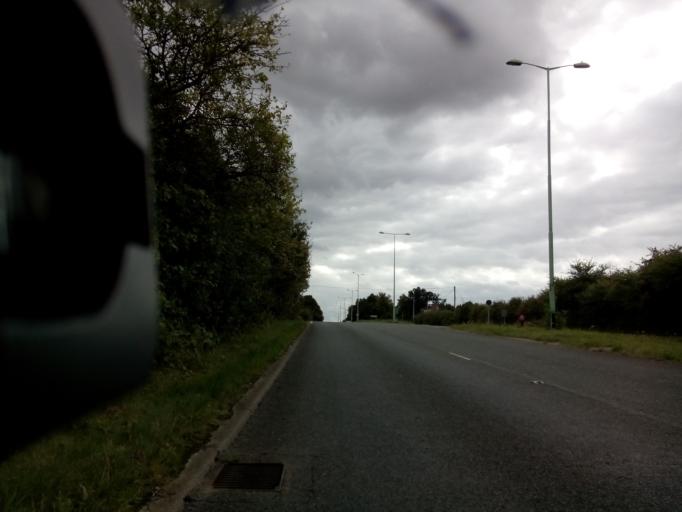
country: GB
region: England
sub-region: Suffolk
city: Bramford
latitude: 52.0324
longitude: 1.0845
